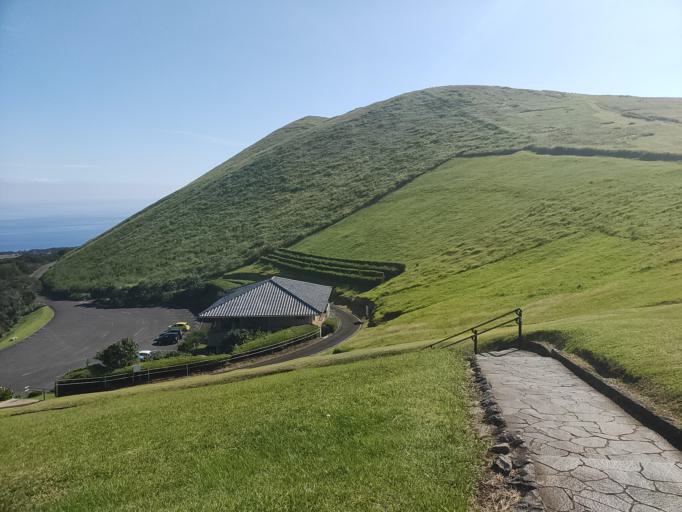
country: JP
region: Nagasaki
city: Fukuecho
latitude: 32.6630
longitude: 128.8506
